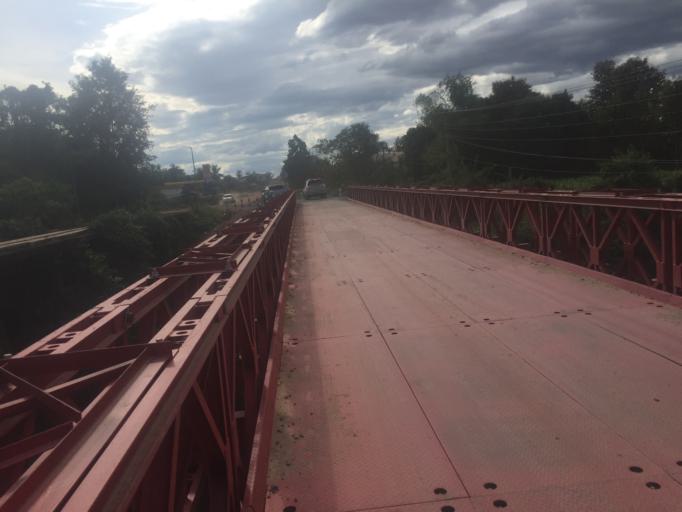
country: LA
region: Attapu
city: Attapu
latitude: 14.6832
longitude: 106.5895
